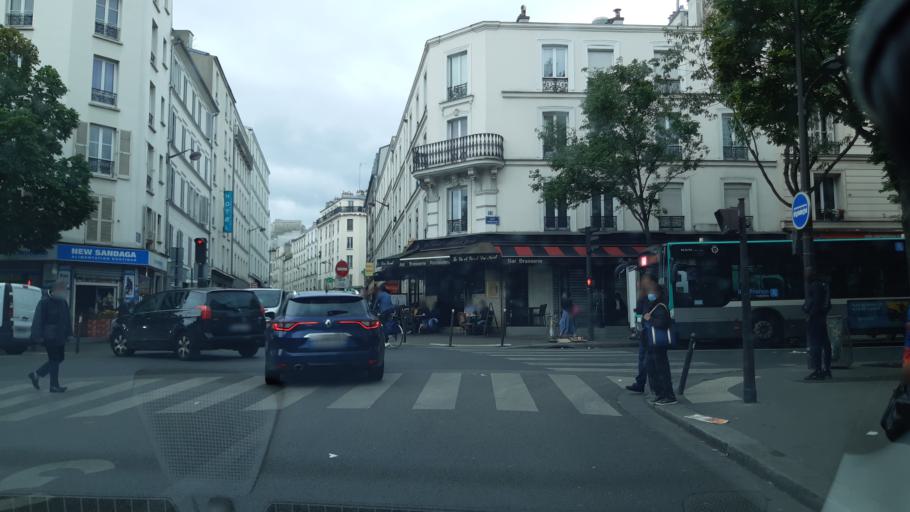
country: FR
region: Ile-de-France
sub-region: Paris
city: Saint-Ouen
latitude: 48.8914
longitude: 2.3516
